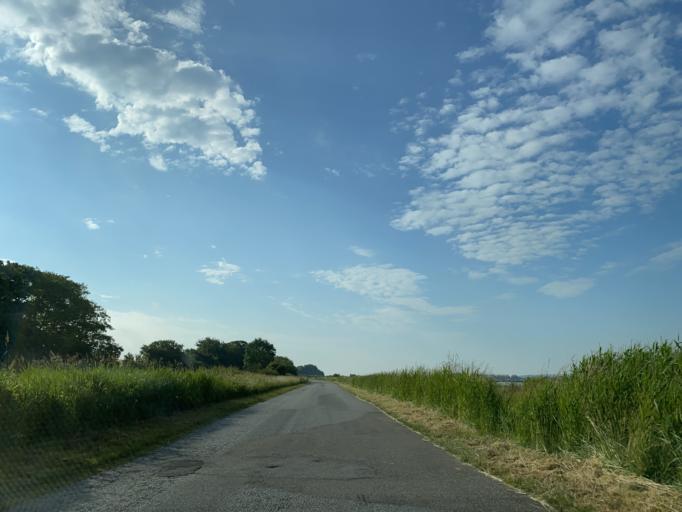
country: DK
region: South Denmark
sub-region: Haderslev Kommune
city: Haderslev
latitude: 55.1724
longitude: 9.4847
